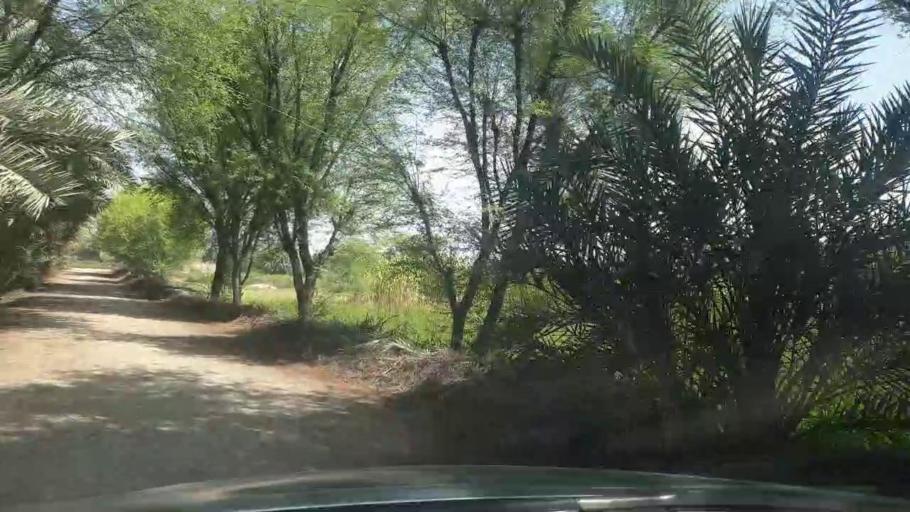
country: PK
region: Sindh
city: Khairpur
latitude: 27.5481
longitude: 68.8019
